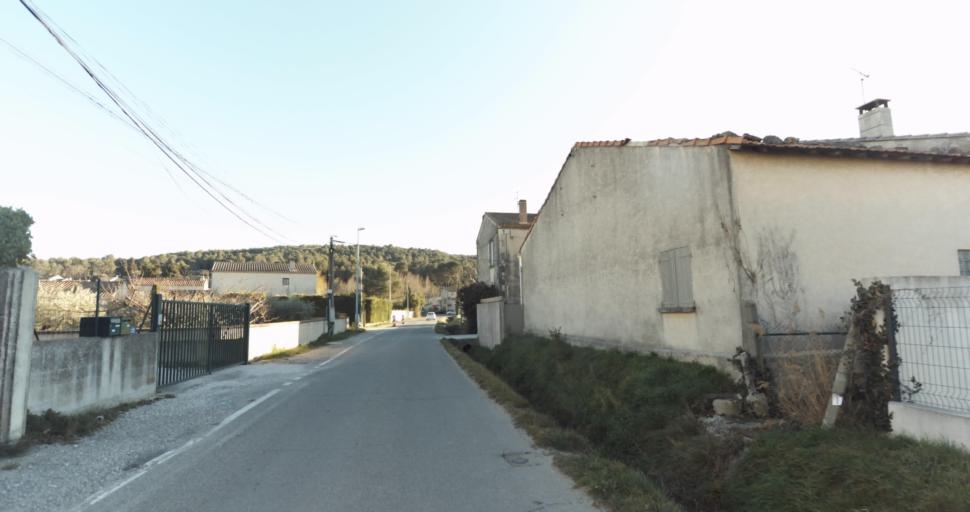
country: FR
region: Provence-Alpes-Cote d'Azur
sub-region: Departement des Bouches-du-Rhone
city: Barbentane
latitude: 43.9037
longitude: 4.7559
